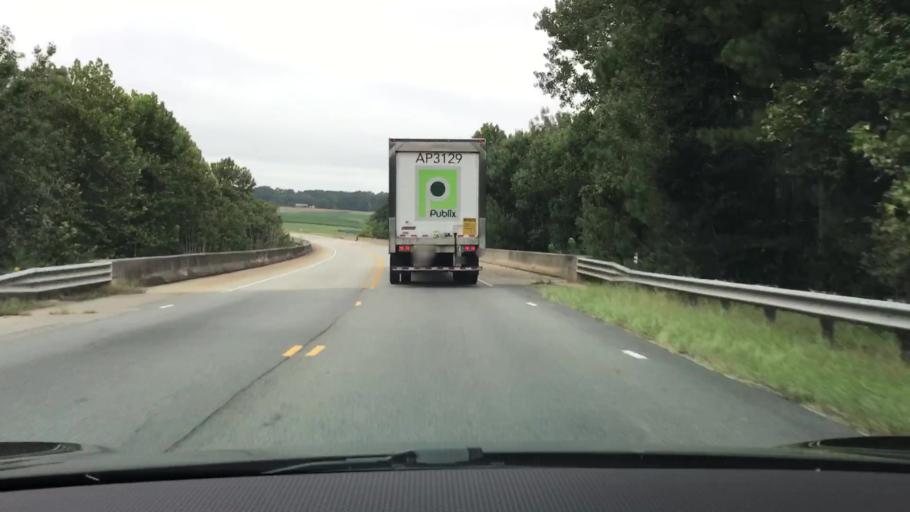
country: US
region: Georgia
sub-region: Greene County
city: Greensboro
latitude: 33.7199
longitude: -83.2944
